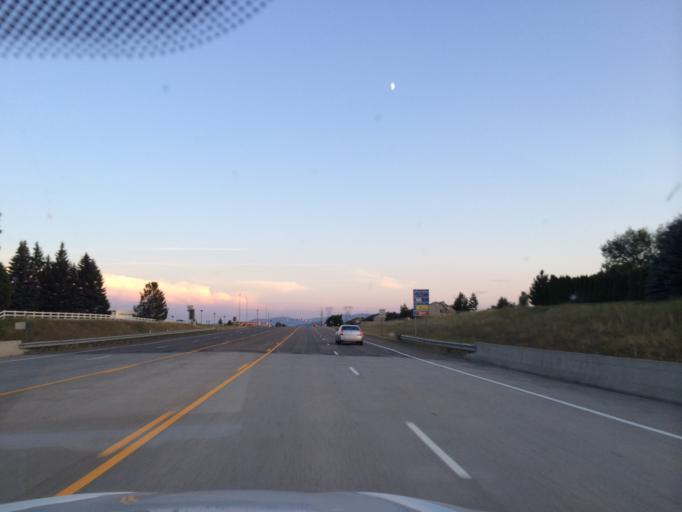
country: US
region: Montana
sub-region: Flathead County
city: Kalispell
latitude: 48.2453
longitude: -114.3306
